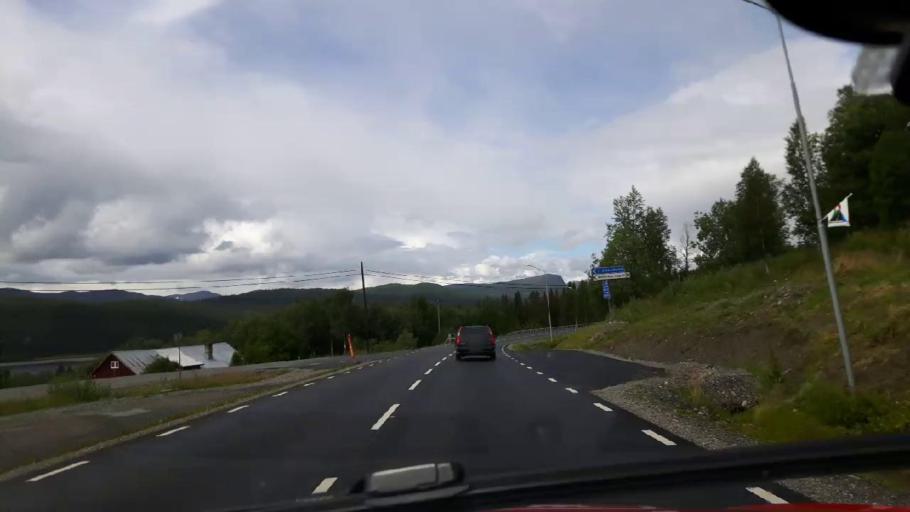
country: NO
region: Nord-Trondelag
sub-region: Royrvik
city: Royrvik
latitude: 64.8309
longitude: 14.1163
